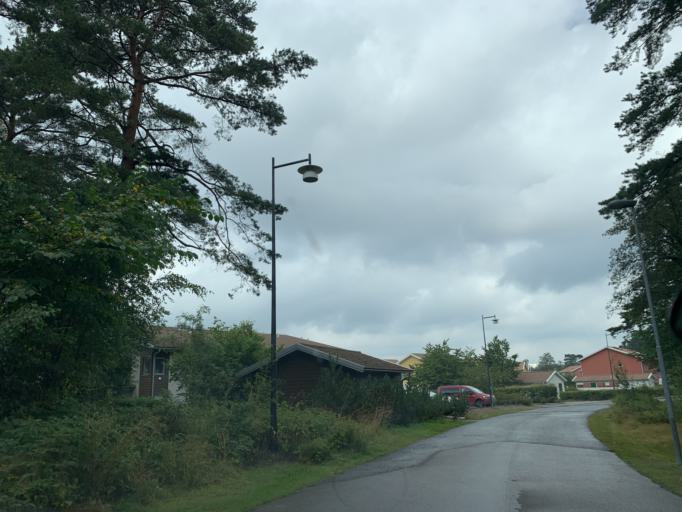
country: SE
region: Vaestra Goetaland
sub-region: Goteborg
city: Eriksbo
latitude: 57.7425
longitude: 12.0341
